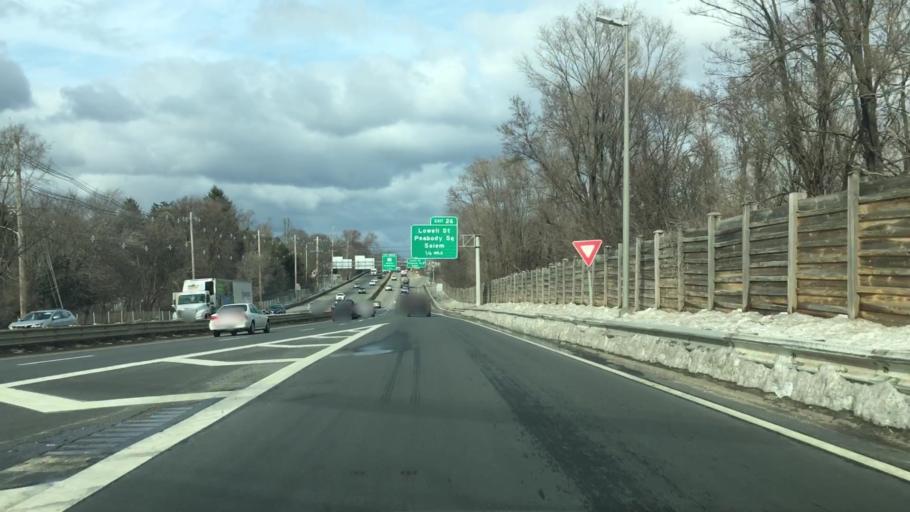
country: US
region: Massachusetts
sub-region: Essex County
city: South Peabody
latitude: 42.5290
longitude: -70.9537
